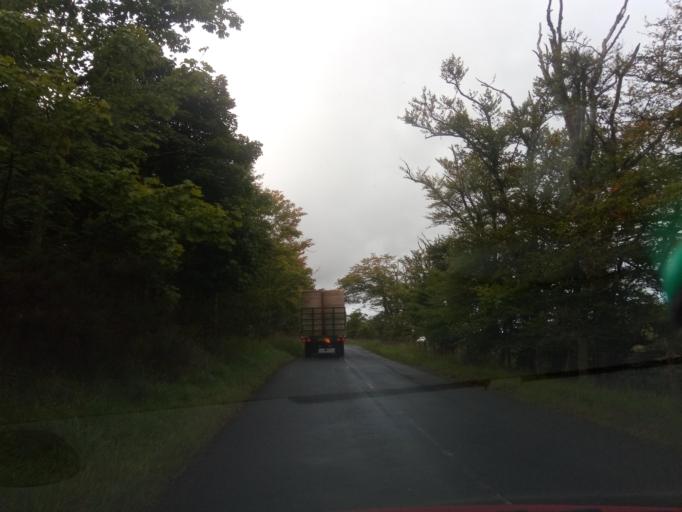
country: GB
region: Scotland
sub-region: The Scottish Borders
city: Duns
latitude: 55.8247
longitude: -2.4235
